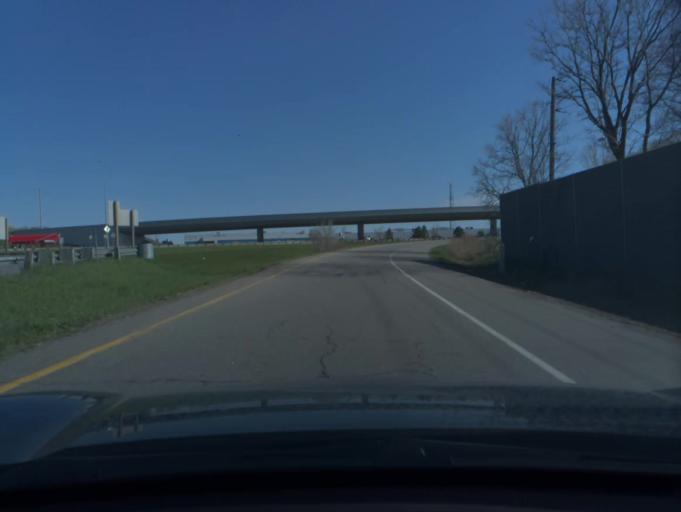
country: CA
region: Ontario
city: North Perth
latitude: 43.8033
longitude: -81.0000
